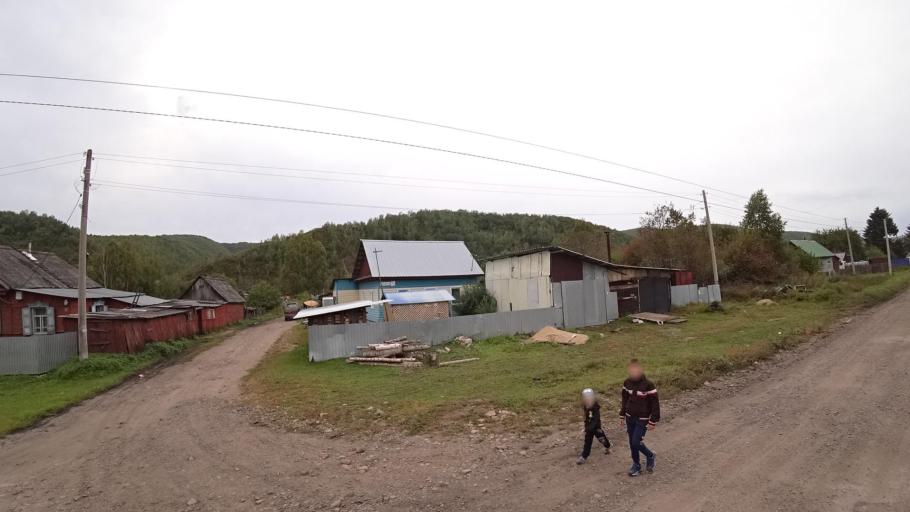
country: RU
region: Jewish Autonomous Oblast
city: Khingansk
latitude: 49.0256
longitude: 131.0480
